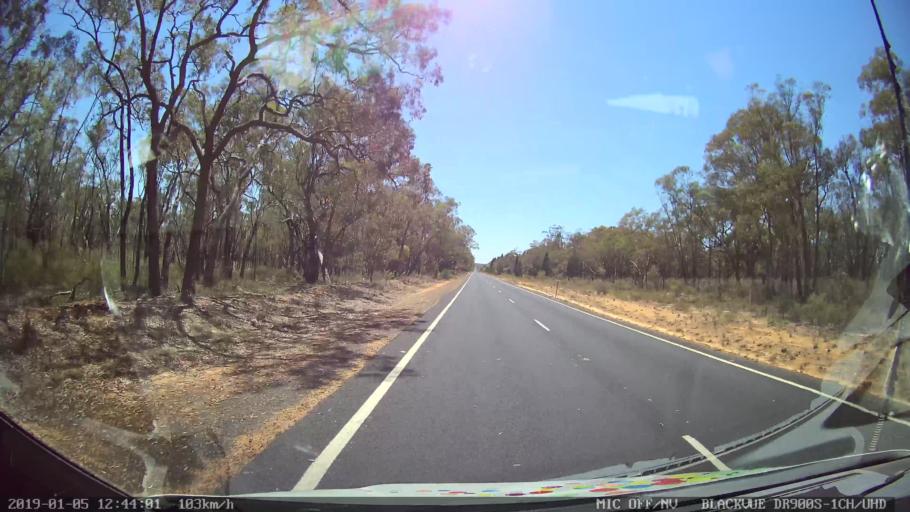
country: AU
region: New South Wales
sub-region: Warrumbungle Shire
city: Coonabarabran
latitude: -31.1420
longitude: 149.5317
